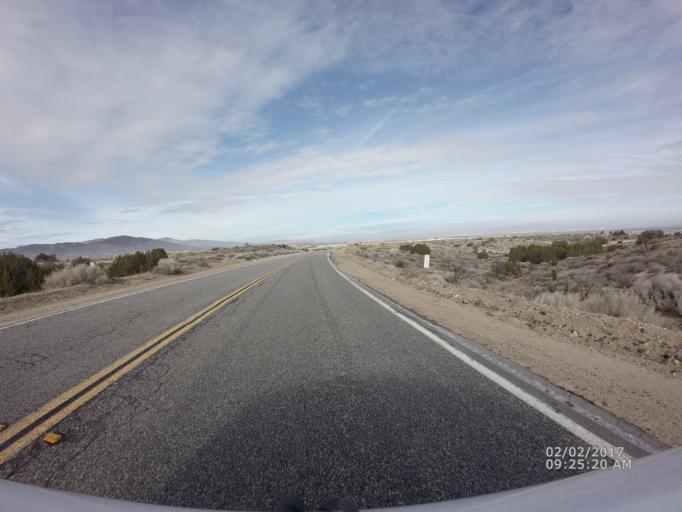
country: US
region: California
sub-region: Los Angeles County
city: Vincent
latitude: 34.5290
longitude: -118.0714
